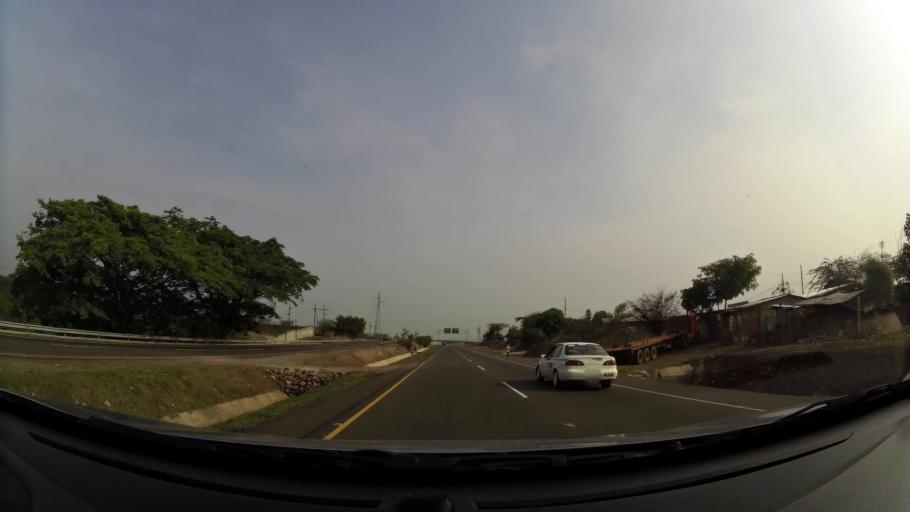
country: HN
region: Comayagua
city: Comayagua
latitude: 14.3970
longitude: -87.6165
